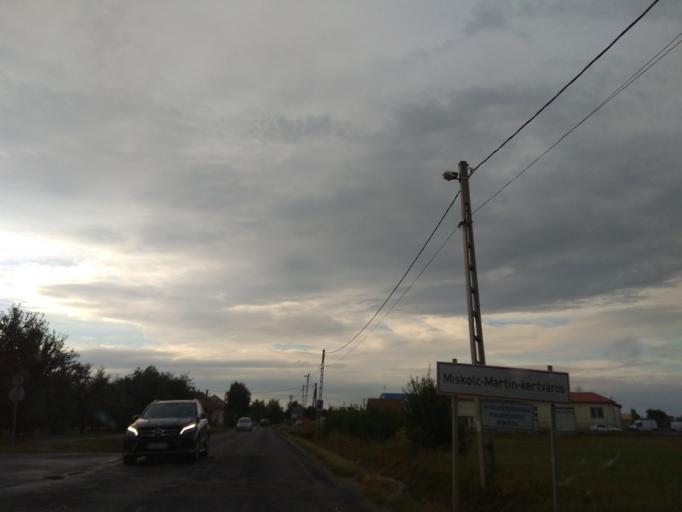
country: HU
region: Borsod-Abauj-Zemplen
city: Miskolc
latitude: 48.0849
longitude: 20.8177
